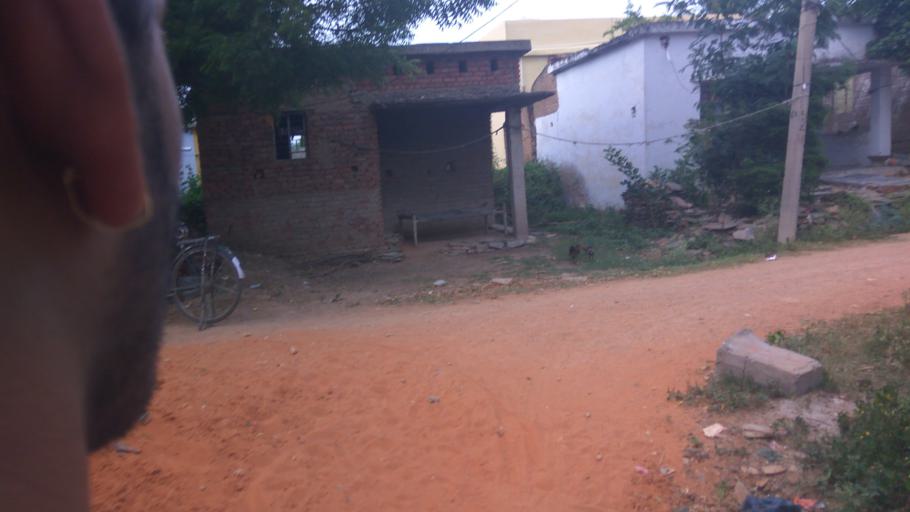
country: IN
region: Andhra Pradesh
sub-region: Prakasam
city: Cumbum
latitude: 15.5905
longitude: 79.1086
